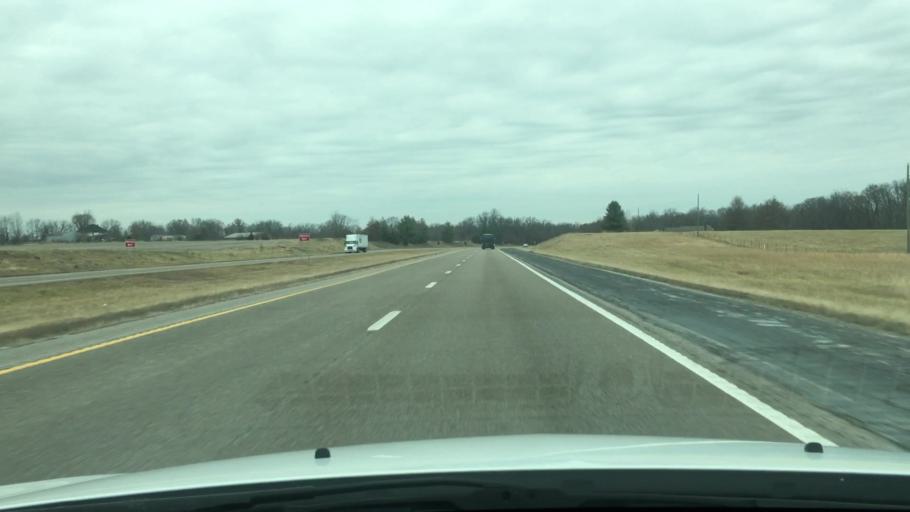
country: US
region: Missouri
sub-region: Audrain County
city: Mexico
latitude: 39.0382
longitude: -91.8912
